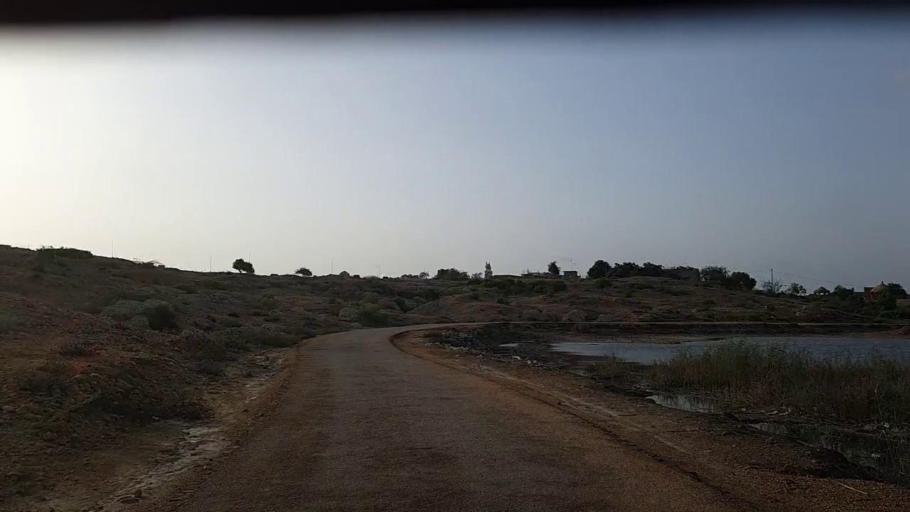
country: PK
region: Sindh
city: Thatta
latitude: 24.7577
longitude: 67.9042
